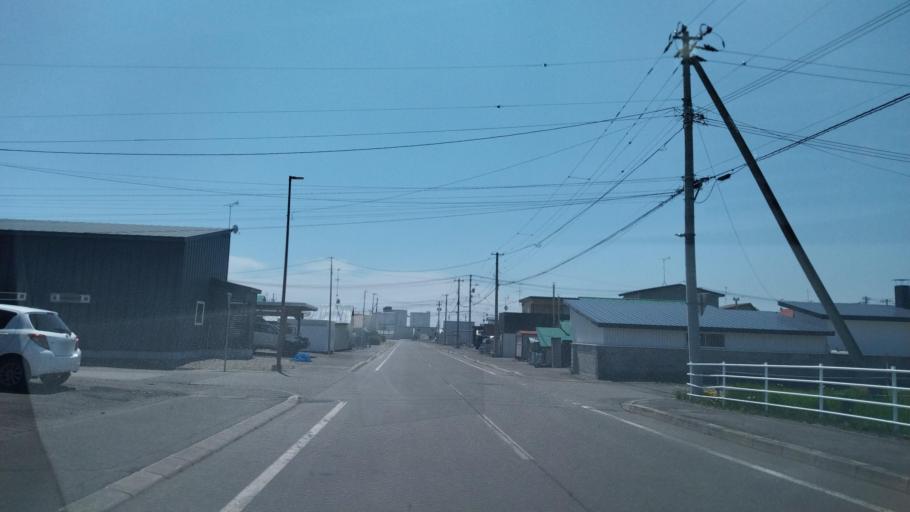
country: JP
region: Hokkaido
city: Otofuke
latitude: 43.1710
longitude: 143.2522
